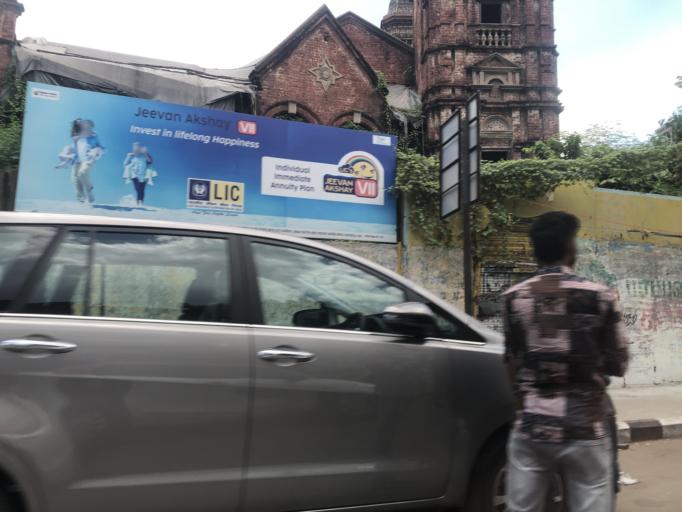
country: IN
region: Tamil Nadu
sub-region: Chennai
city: Chennai
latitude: 13.0649
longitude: 80.2676
